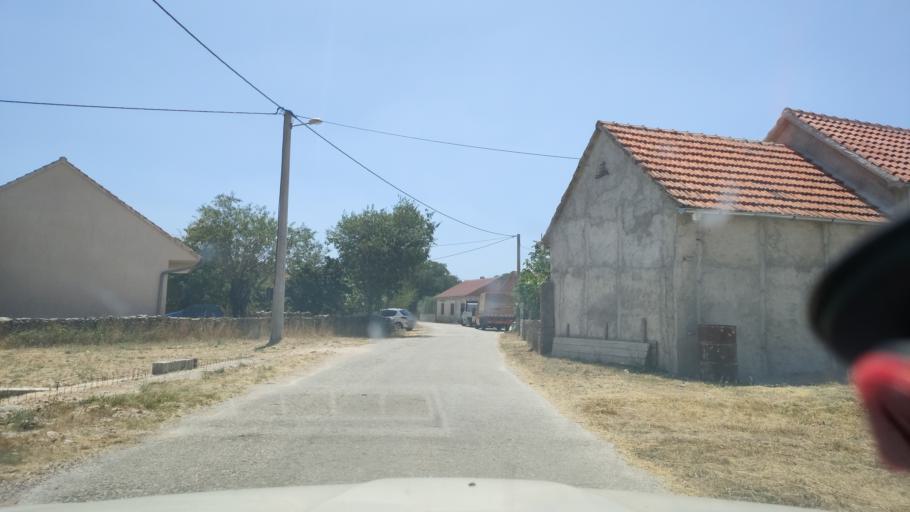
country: HR
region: Sibensko-Kniniska
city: Kistanje
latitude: 43.9602
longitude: 15.8738
